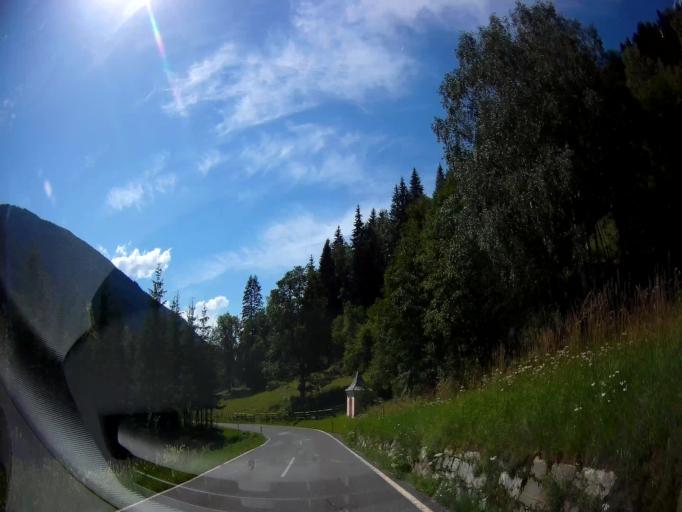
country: AT
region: Salzburg
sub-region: Politischer Bezirk Tamsweg
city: Thomatal
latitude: 47.0639
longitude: 13.7733
